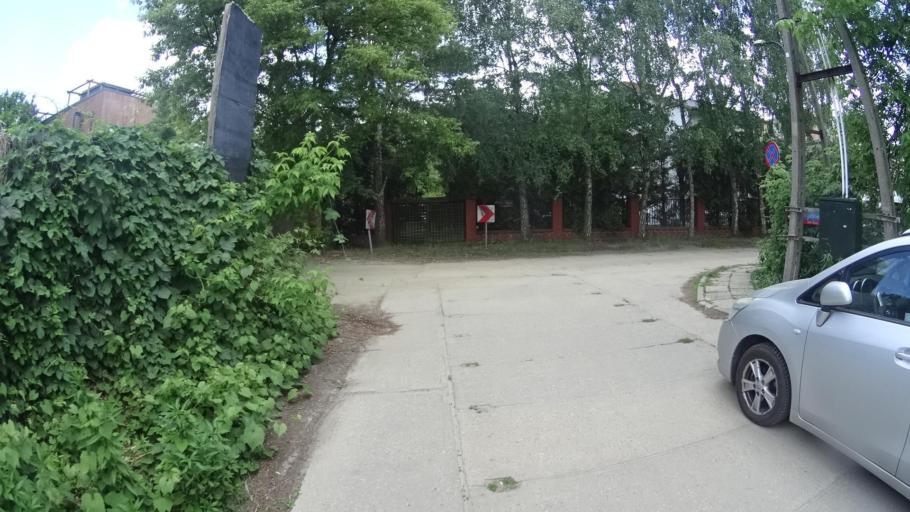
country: PL
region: Masovian Voivodeship
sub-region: Warszawa
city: Wlochy
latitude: 52.2076
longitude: 20.9273
